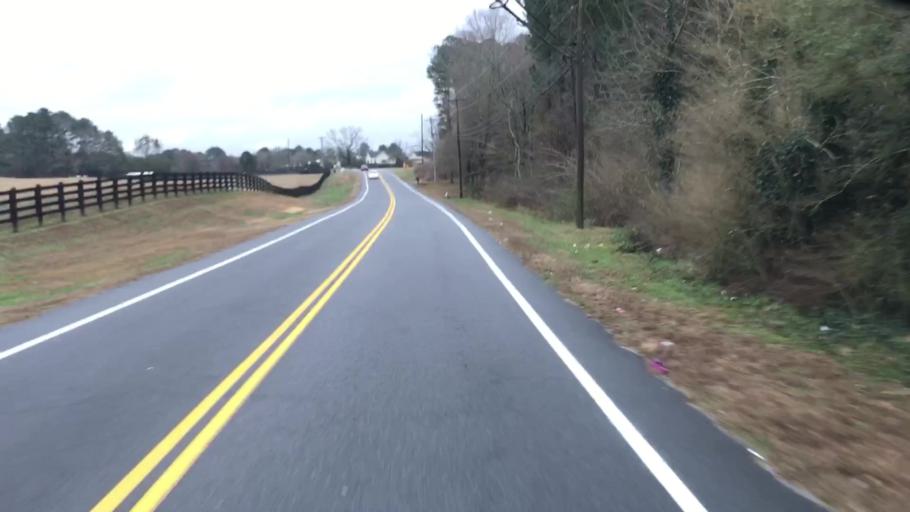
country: US
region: Georgia
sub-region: Gwinnett County
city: Snellville
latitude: 33.8170
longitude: -83.9690
